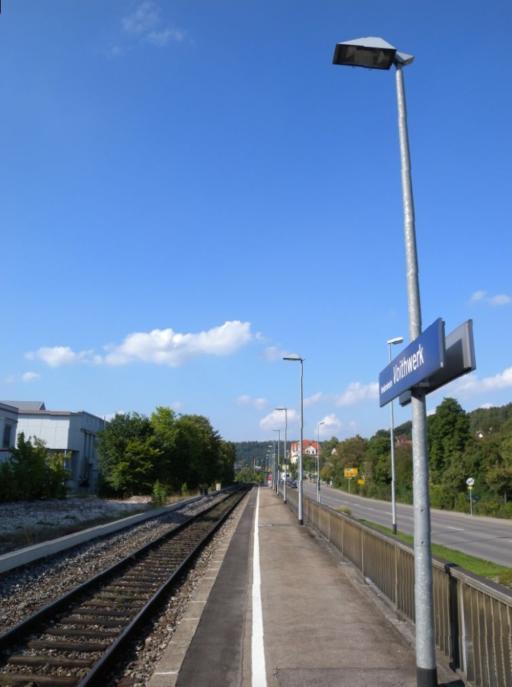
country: DE
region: Baden-Wuerttemberg
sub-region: Regierungsbezirk Stuttgart
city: Heidenheim an der Brenz
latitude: 48.6686
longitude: 10.1555
